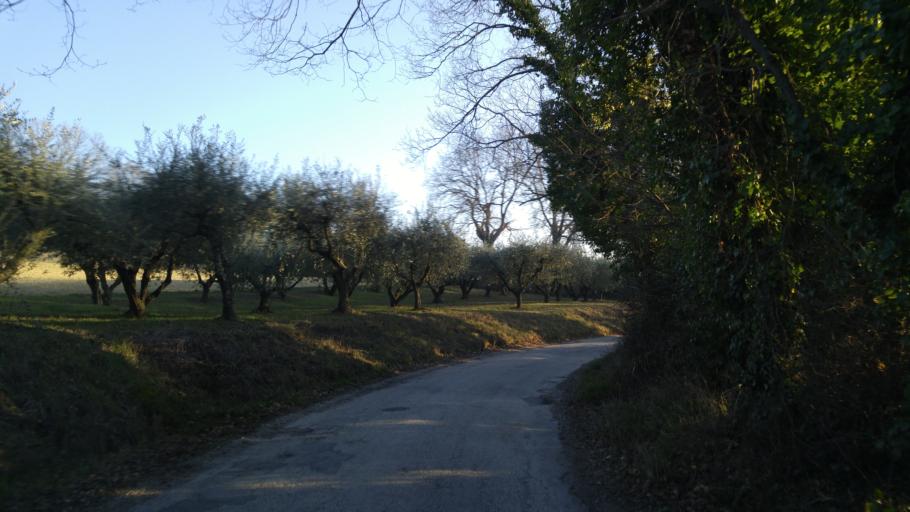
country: IT
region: The Marches
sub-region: Provincia di Pesaro e Urbino
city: Fenile
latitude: 43.8608
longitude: 12.9559
